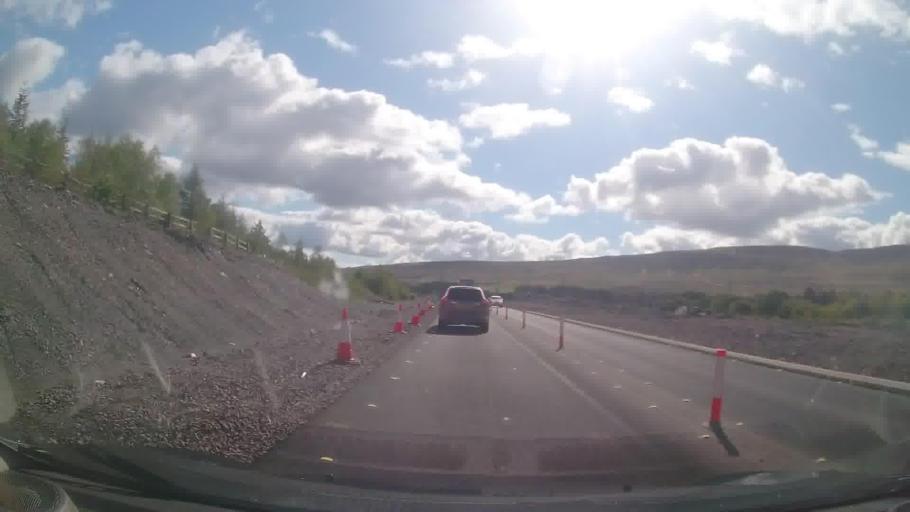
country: GB
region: Wales
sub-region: Rhondda Cynon Taf
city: Hirwaun
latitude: 51.7411
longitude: -3.5252
